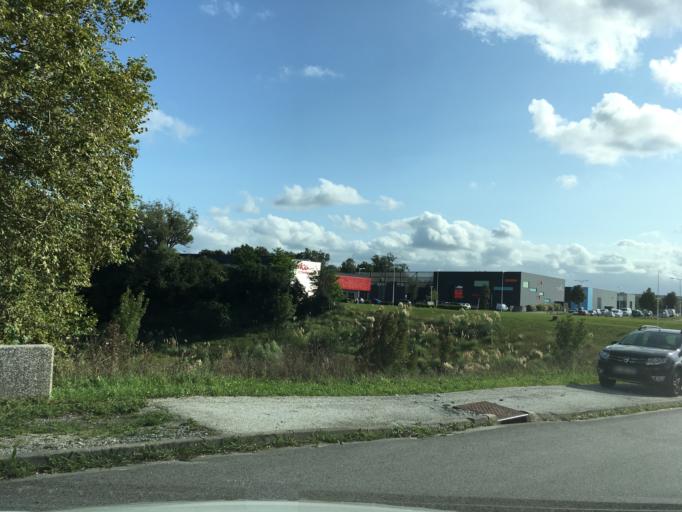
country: FR
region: Aquitaine
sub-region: Departement des Pyrenees-Atlantiques
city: Bayonne
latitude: 43.4677
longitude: -1.4907
